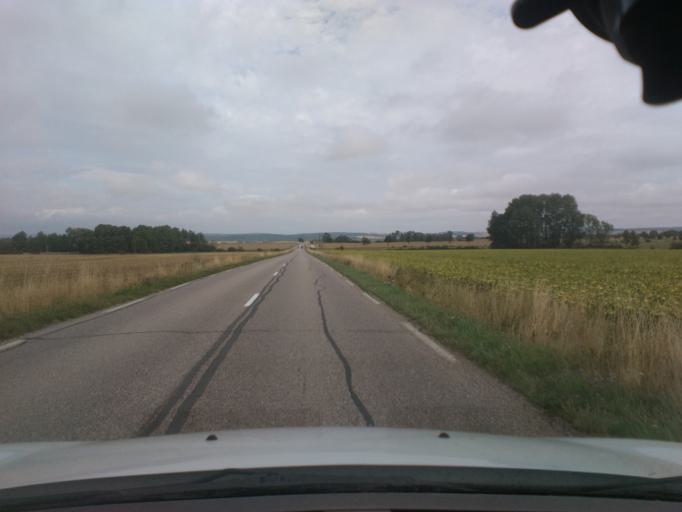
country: FR
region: Lorraine
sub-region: Departement de Meurthe-et-Moselle
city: Vezelise
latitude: 48.4849
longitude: 6.1434
